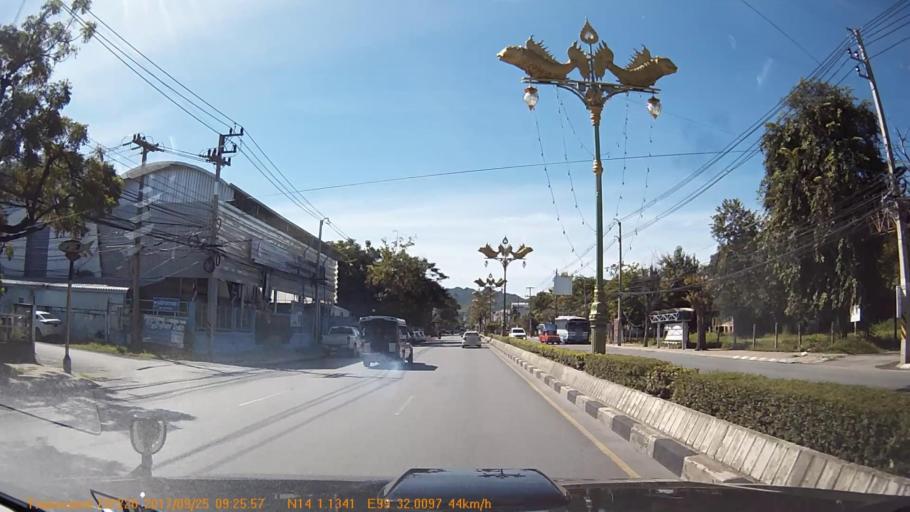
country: TH
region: Kanchanaburi
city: Kanchanaburi
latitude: 14.0188
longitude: 99.5335
